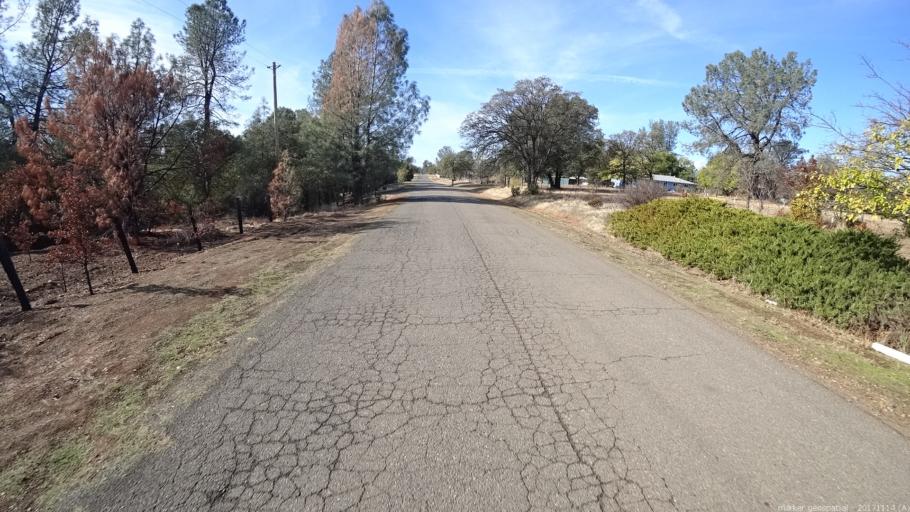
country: US
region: California
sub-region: Shasta County
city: Anderson
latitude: 40.4247
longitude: -122.3980
